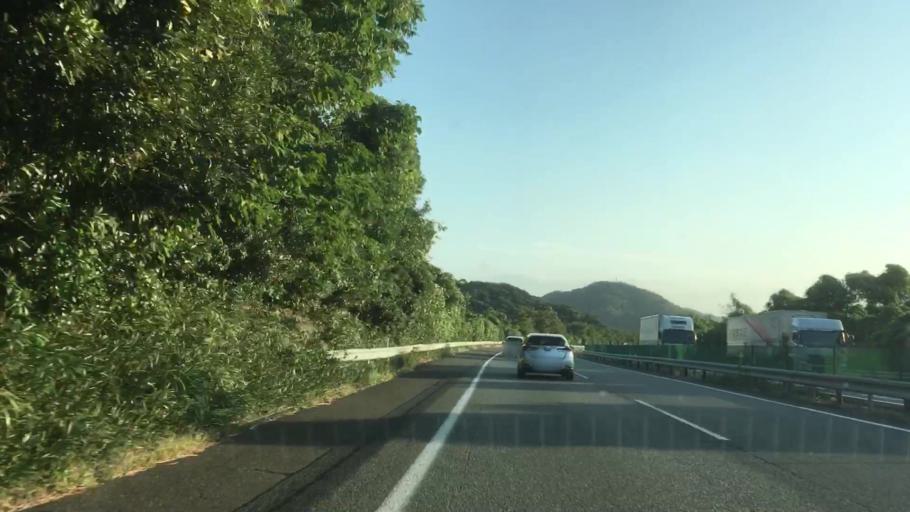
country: JP
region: Yamaguchi
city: Shimonoseki
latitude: 34.0182
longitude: 130.9578
